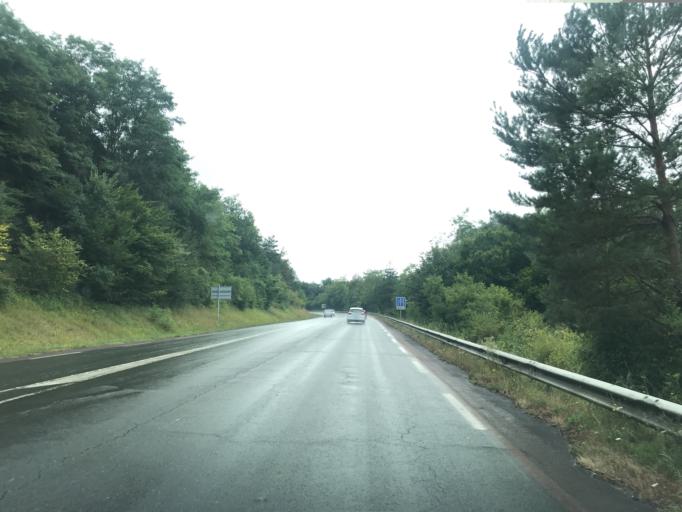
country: FR
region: Aquitaine
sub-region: Departement de la Dordogne
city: Brantome
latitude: 45.3389
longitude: 0.6515
